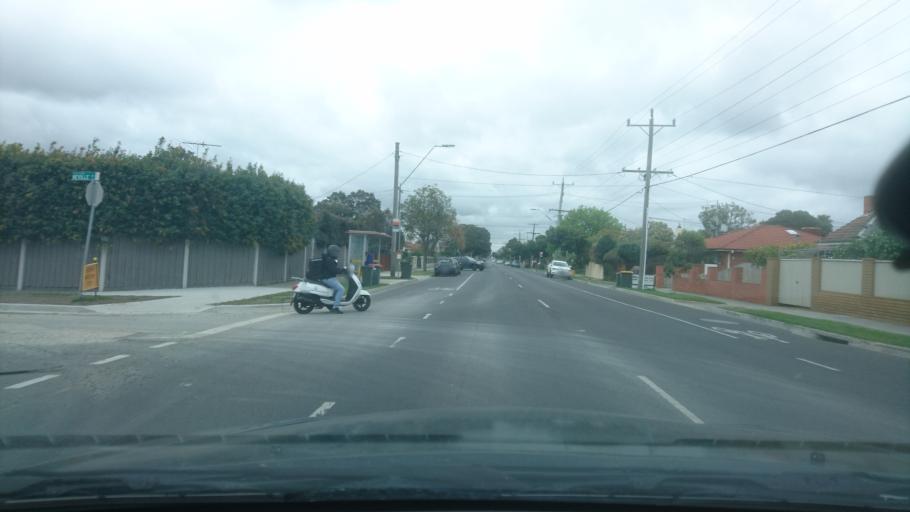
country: AU
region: Victoria
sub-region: Glen Eira
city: Carnegie
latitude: -37.8983
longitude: 145.0553
